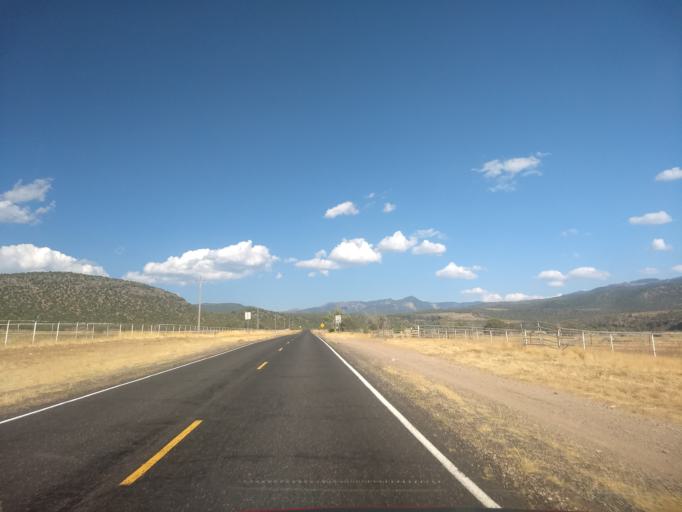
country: US
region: Utah
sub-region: Washington County
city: Enterprise
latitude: 37.4170
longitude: -113.6161
